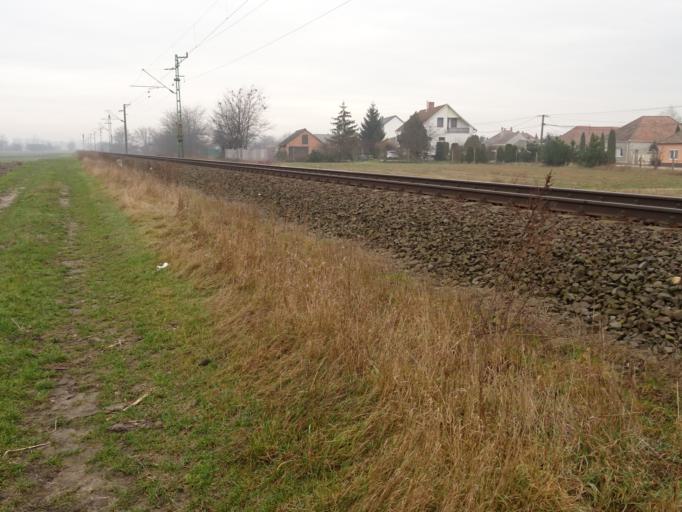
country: HU
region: Gyor-Moson-Sopron
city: Kony
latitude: 47.6351
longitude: 17.3682
